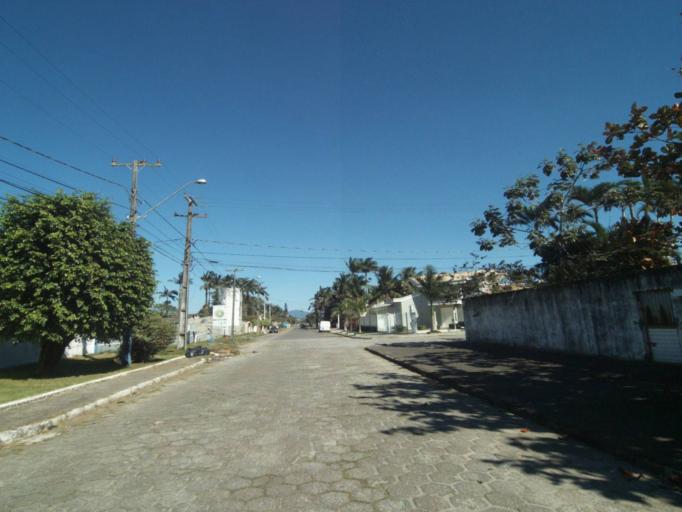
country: BR
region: Parana
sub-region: Paranagua
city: Paranagua
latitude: -25.5138
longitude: -48.4990
